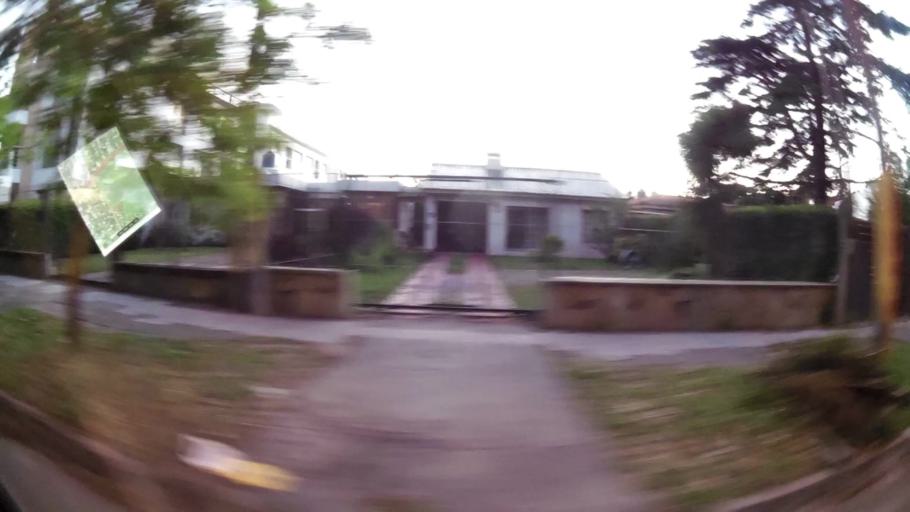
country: UY
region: Canelones
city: Paso de Carrasco
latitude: -34.8830
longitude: -56.0972
